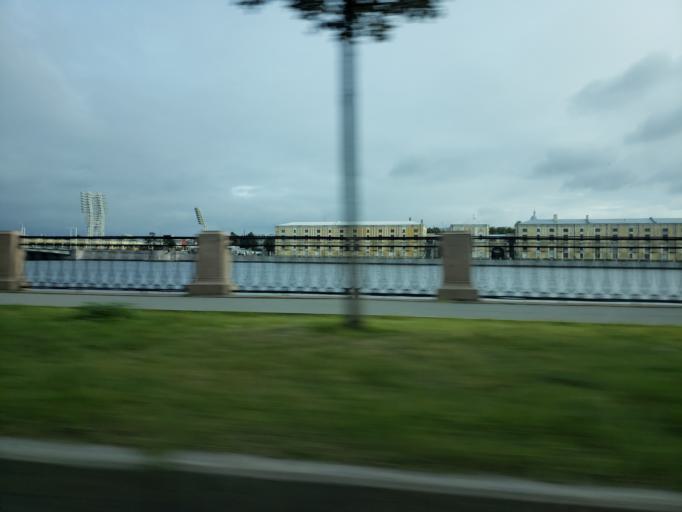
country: RU
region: St.-Petersburg
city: Saint Petersburg
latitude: 59.9468
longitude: 30.2879
